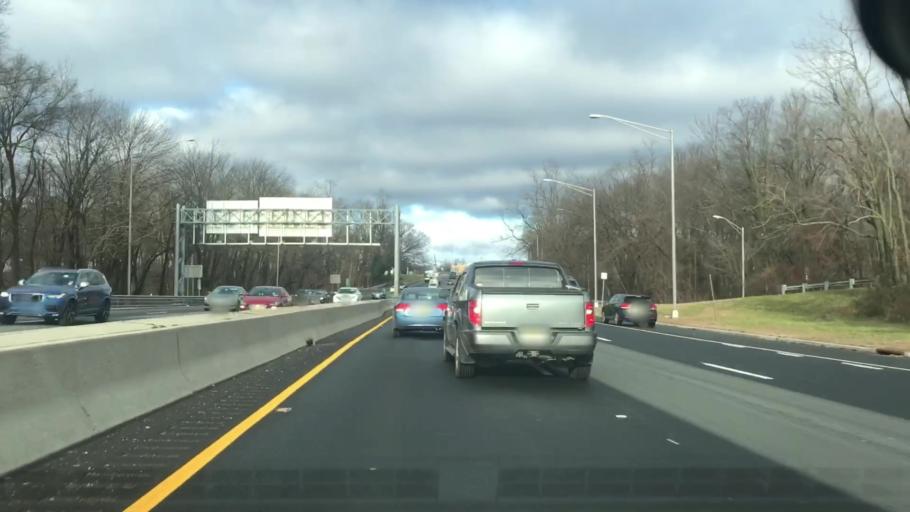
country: US
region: New Jersey
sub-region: Bergen County
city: Ho-Ho-Kus
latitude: 40.9838
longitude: -74.0898
